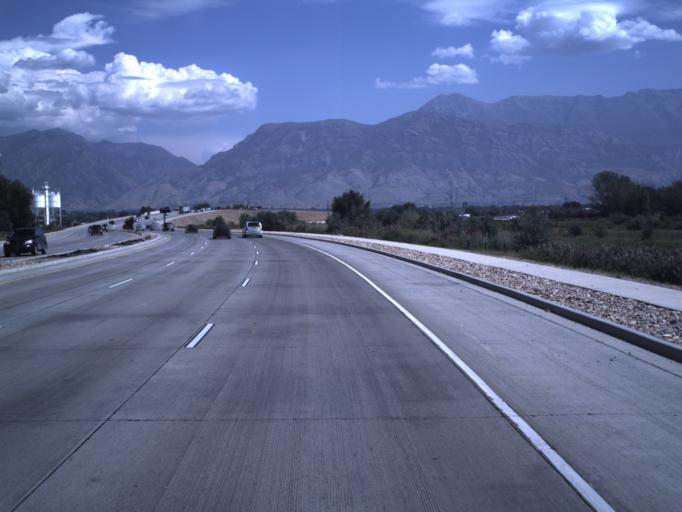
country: US
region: Utah
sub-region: Utah County
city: Lehi
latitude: 40.3740
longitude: -111.8393
